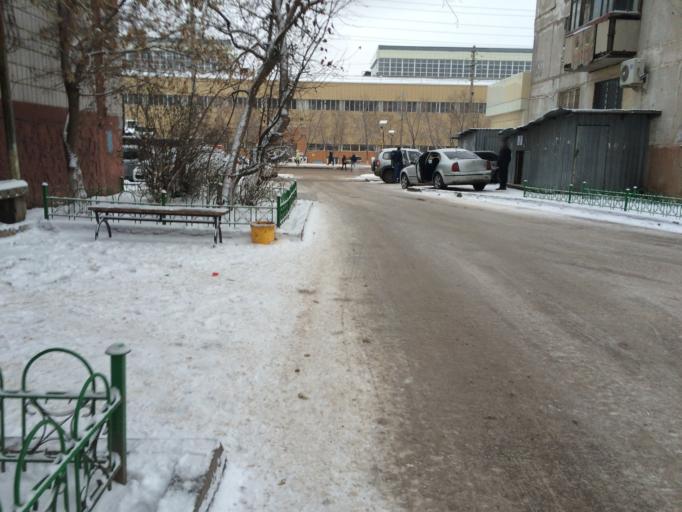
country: KZ
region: Astana Qalasy
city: Astana
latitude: 51.1801
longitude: 71.4337
